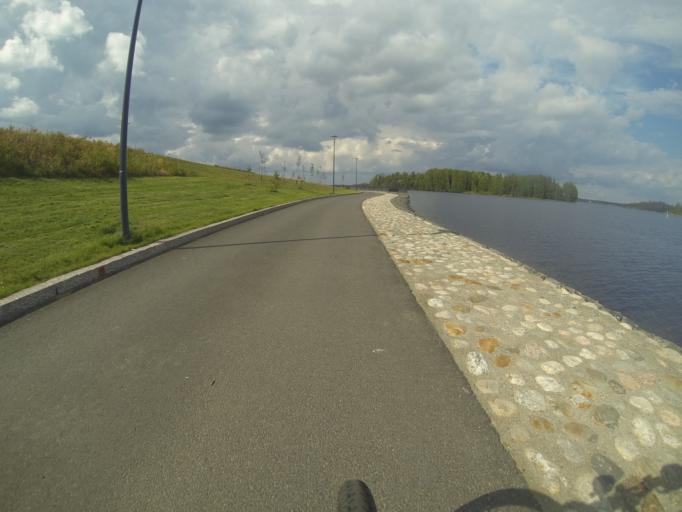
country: FI
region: Southern Savonia
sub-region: Savonlinna
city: Savonlinna
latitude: 61.8731
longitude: 28.8817
